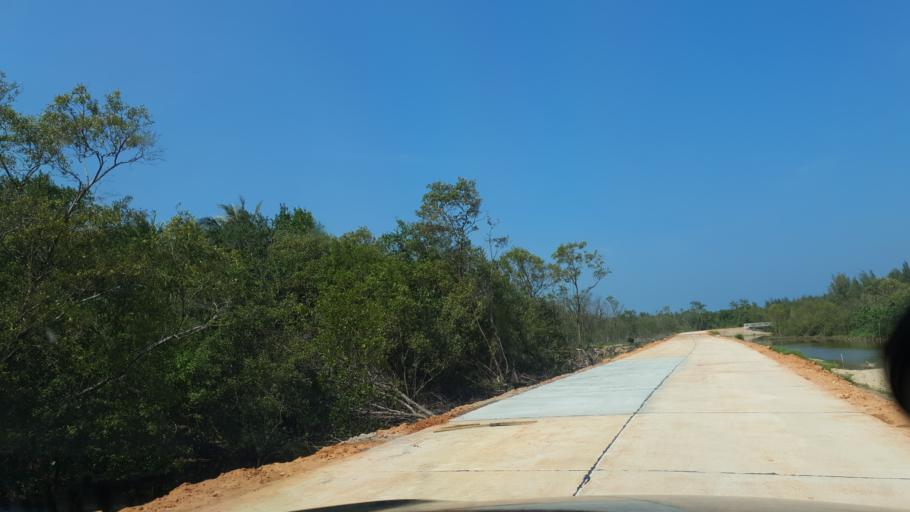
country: TH
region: Surat Thani
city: Tha Chana
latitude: 9.5921
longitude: 99.2076
